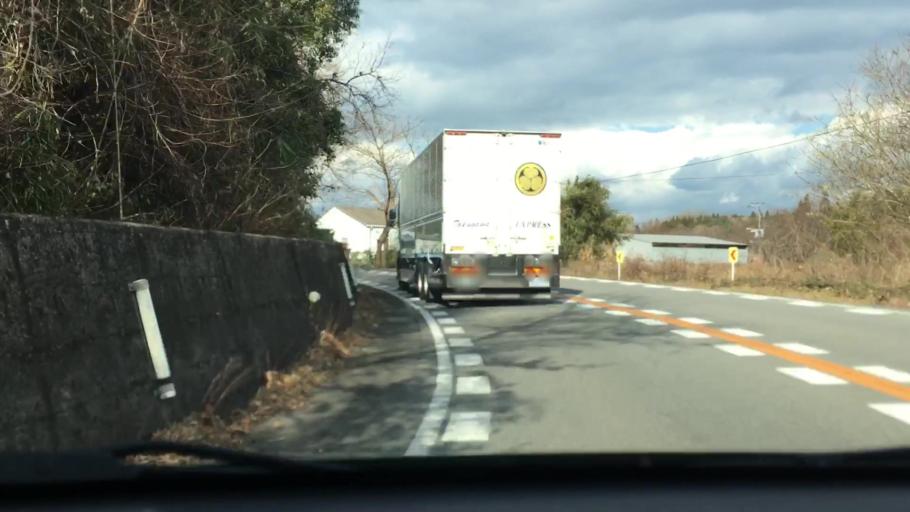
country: JP
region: Oita
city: Usuki
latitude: 33.0275
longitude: 131.6948
